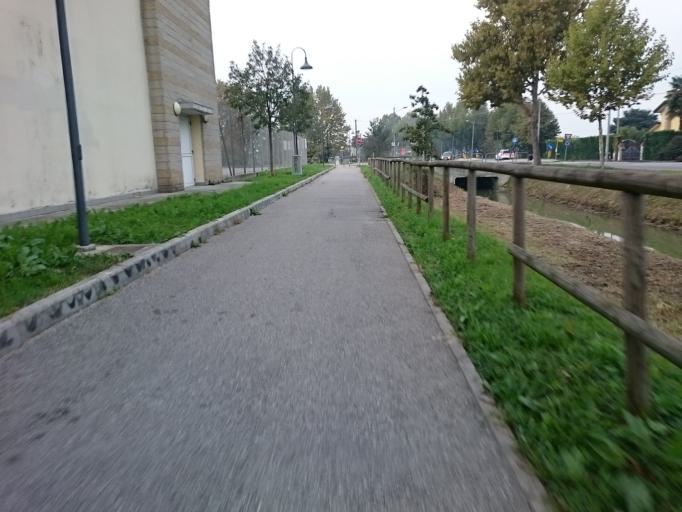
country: IT
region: Veneto
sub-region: Provincia di Padova
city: Albignasego
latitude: 45.3627
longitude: 11.8921
